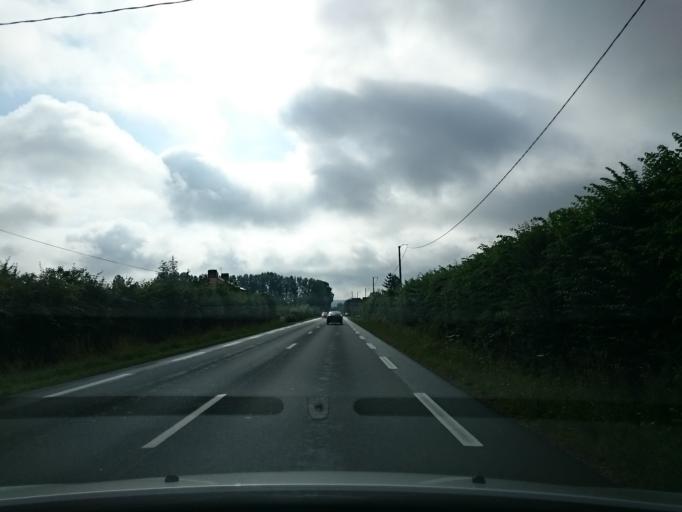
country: FR
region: Lower Normandy
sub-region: Departement du Calvados
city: Cambremer
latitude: 49.1158
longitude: 0.0329
